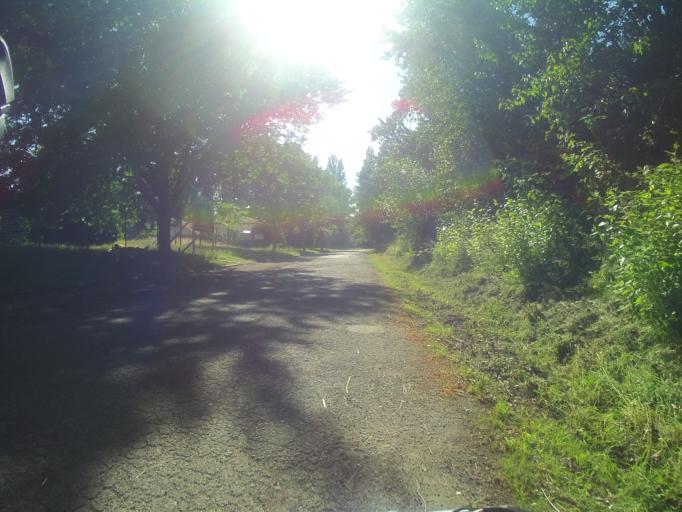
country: CA
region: British Columbia
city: Vancouver
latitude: 49.2178
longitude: -123.1153
